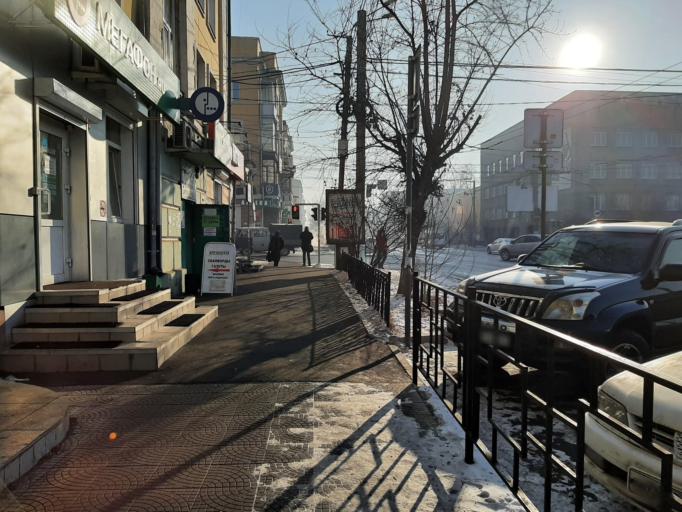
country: RU
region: Transbaikal Territory
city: Chita
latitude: 52.0302
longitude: 113.4988
